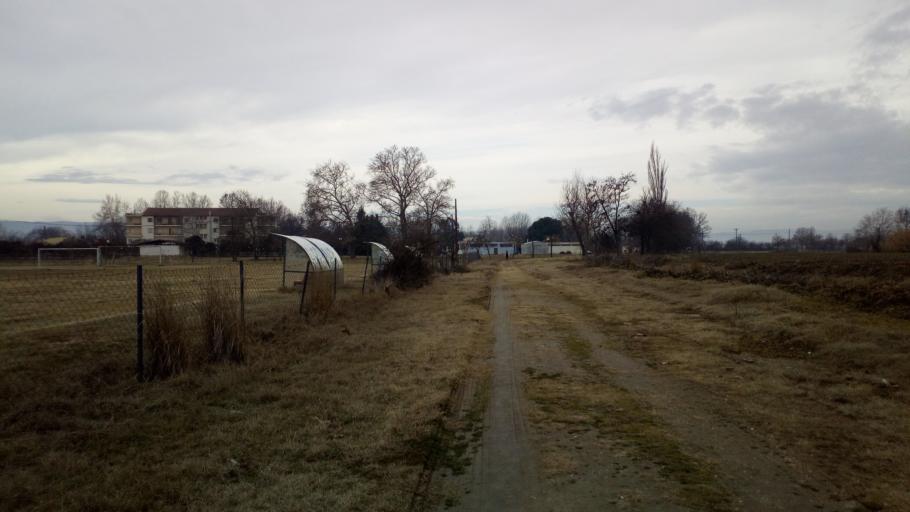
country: GR
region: Central Macedonia
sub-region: Nomos Thessalonikis
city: Lagkadas
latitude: 40.7347
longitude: 23.0881
